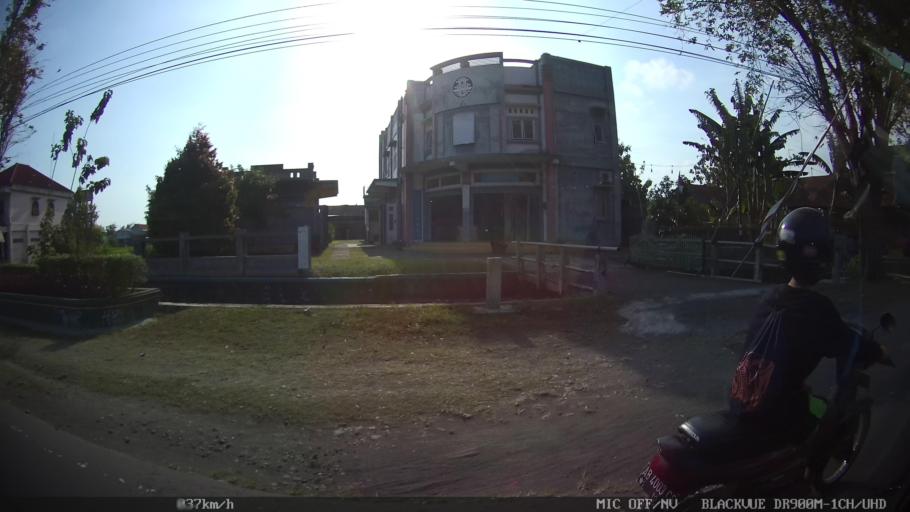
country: ID
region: Daerah Istimewa Yogyakarta
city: Bantul
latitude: -7.8948
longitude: 110.3242
